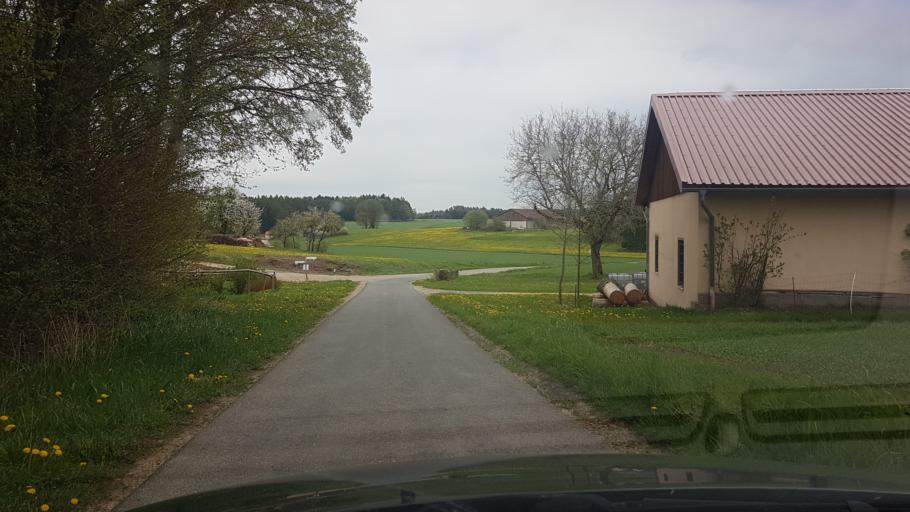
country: DE
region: Bavaria
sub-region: Upper Franconia
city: Wattendorf
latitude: 50.0083
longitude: 11.1553
